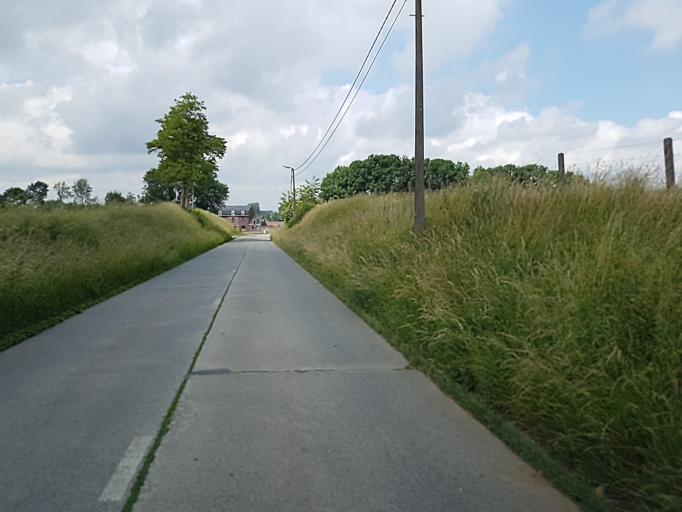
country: BE
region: Flanders
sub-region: Provincie Vlaams-Brabant
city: Herne
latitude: 50.7280
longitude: 4.0874
